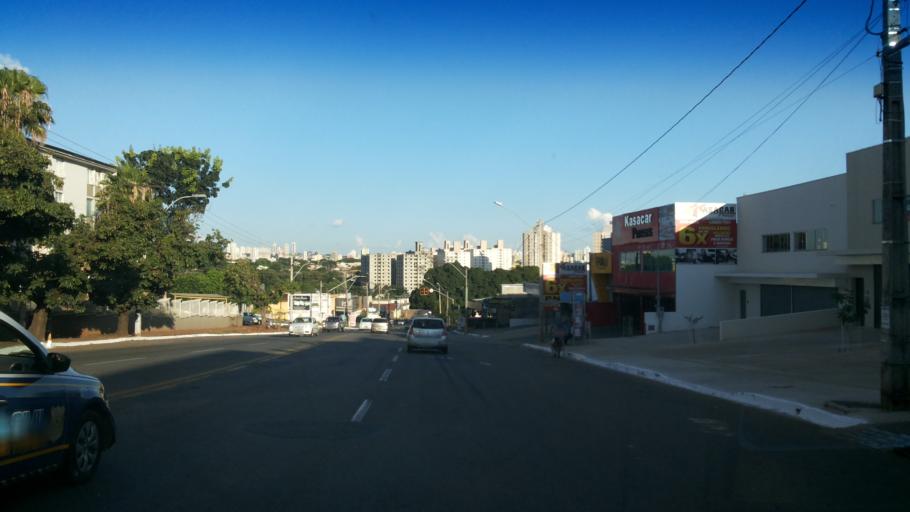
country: BR
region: Goias
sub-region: Goiania
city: Goiania
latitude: -16.6466
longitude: -49.2766
